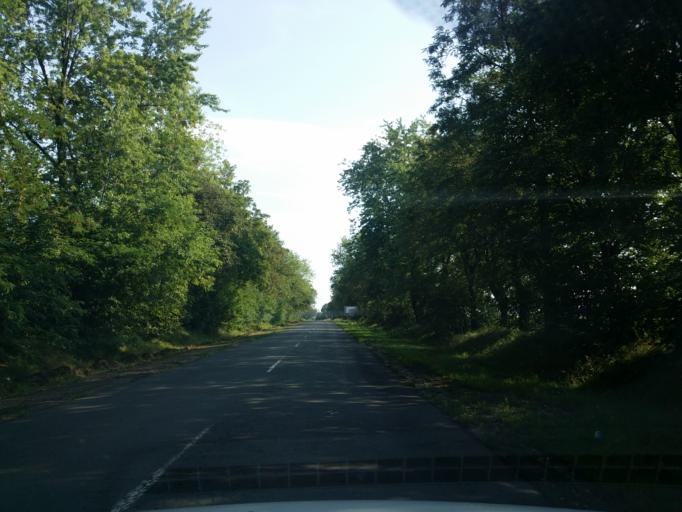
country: HU
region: Borsod-Abauj-Zemplen
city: Abaujszanto
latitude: 48.3527
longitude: 21.2133
